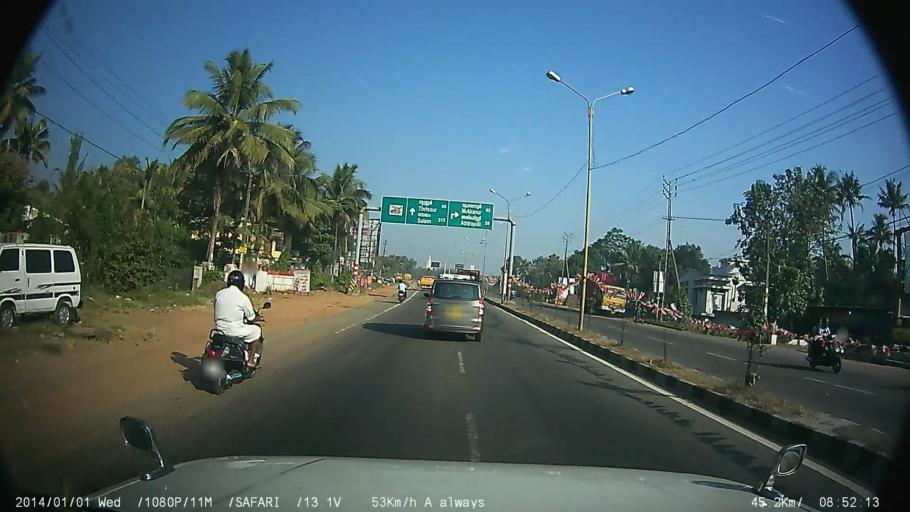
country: IN
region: Kerala
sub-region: Ernakulam
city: Angamali
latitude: 10.2041
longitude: 76.3826
